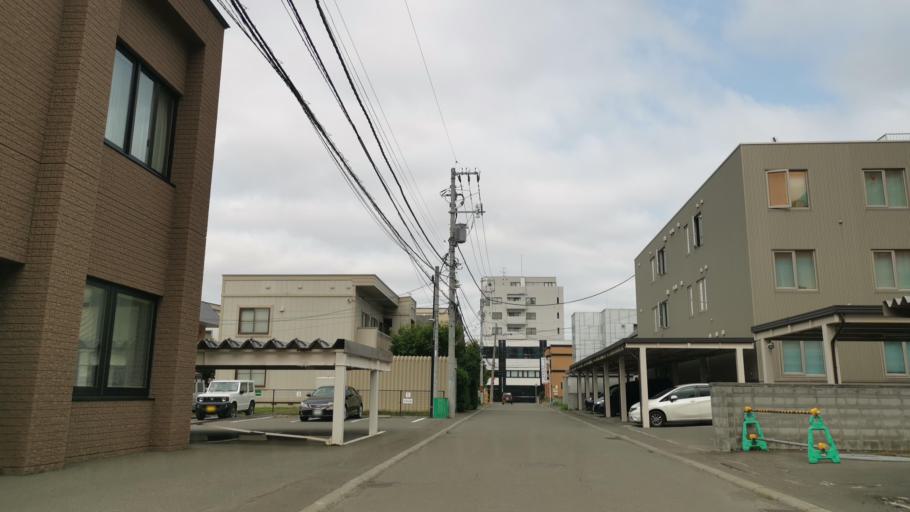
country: JP
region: Hokkaido
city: Sapporo
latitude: 43.0469
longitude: 141.3360
